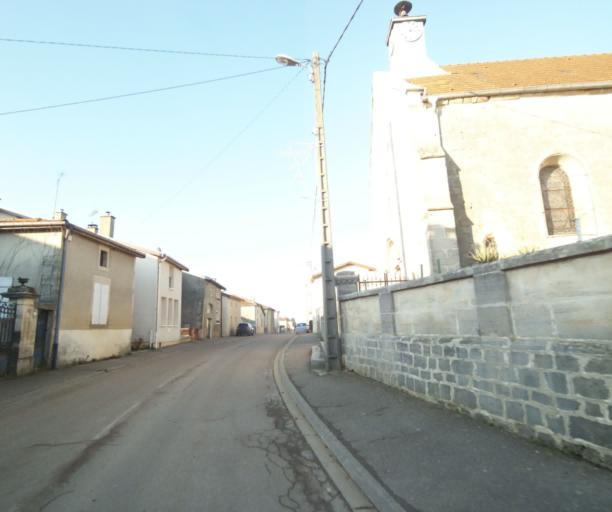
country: FR
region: Champagne-Ardenne
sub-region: Departement de la Haute-Marne
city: Bienville
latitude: 48.5830
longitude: 5.0874
